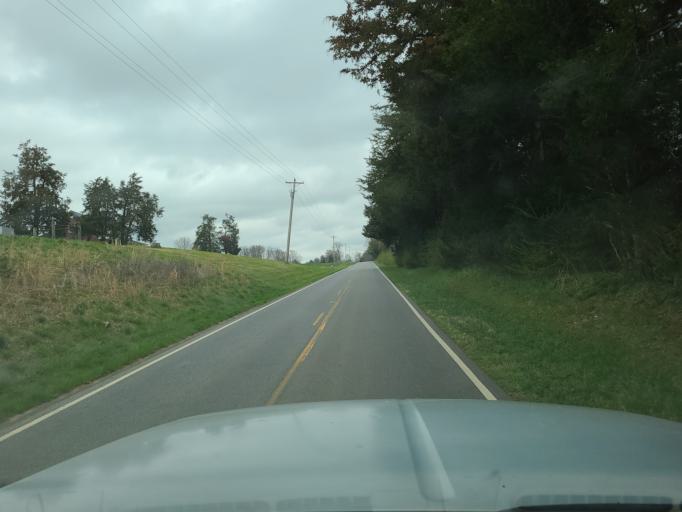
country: US
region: North Carolina
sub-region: Cleveland County
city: Shelby
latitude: 35.4565
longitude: -81.6387
